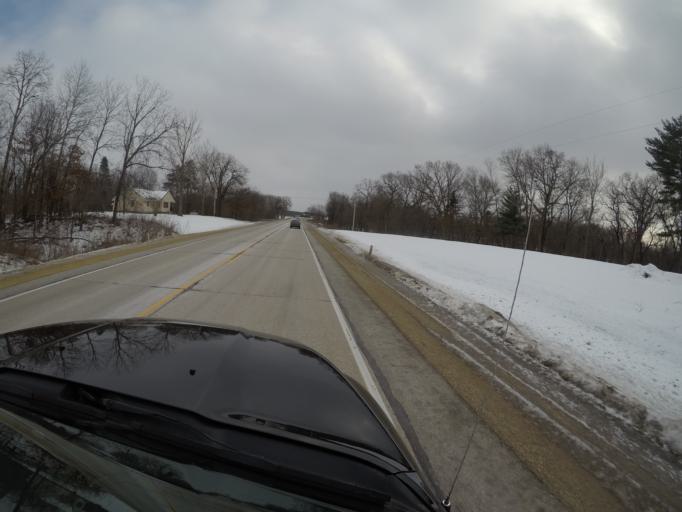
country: US
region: Wisconsin
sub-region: Trempealeau County
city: Galesville
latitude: 44.0711
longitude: -91.3008
